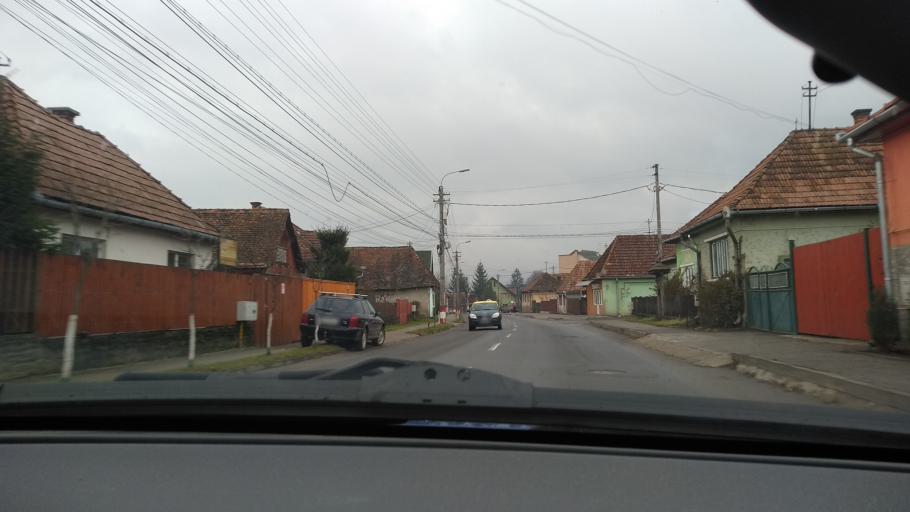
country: RO
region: Mures
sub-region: Oras Sovata
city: Sovata
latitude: 46.5857
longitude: 25.0632
